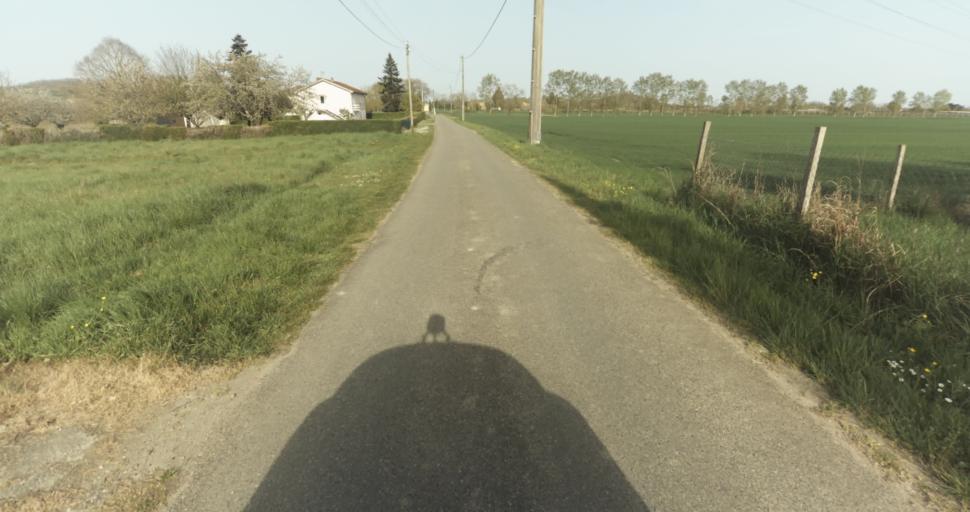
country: FR
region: Midi-Pyrenees
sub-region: Departement du Tarn-et-Garonne
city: Moissac
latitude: 44.1147
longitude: 1.1228
